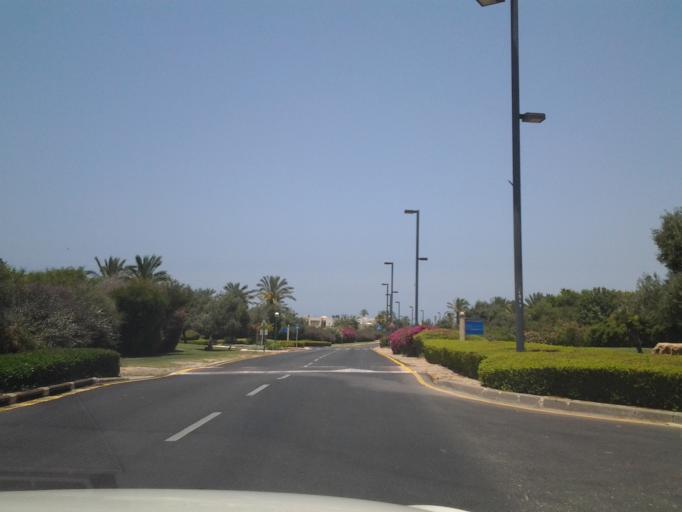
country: IL
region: Haifa
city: Qesarya
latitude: 32.5272
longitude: 34.9080
